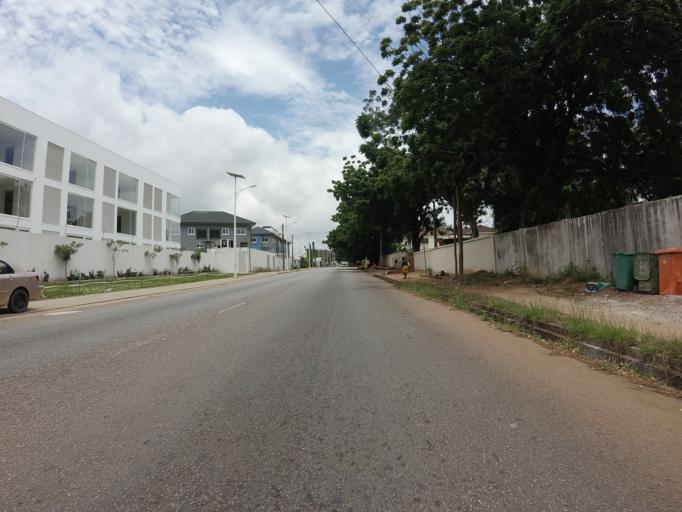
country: GH
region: Greater Accra
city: Accra
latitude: 5.5782
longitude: -0.1773
